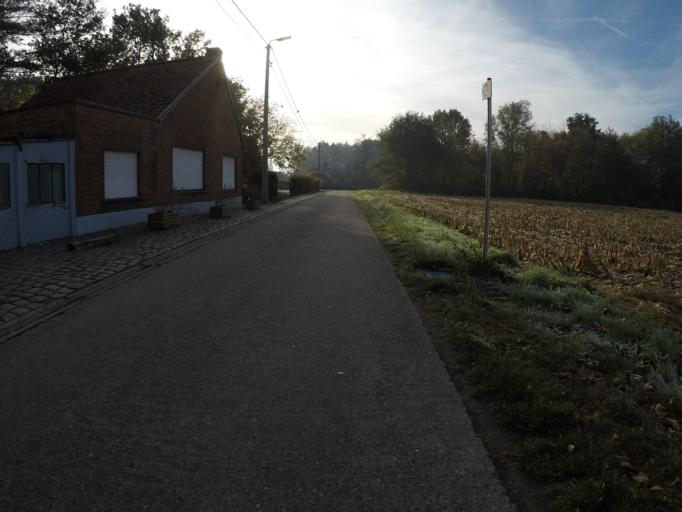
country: BE
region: Flanders
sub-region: Provincie Vlaams-Brabant
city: Begijnendijk
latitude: 51.0124
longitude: 4.7657
